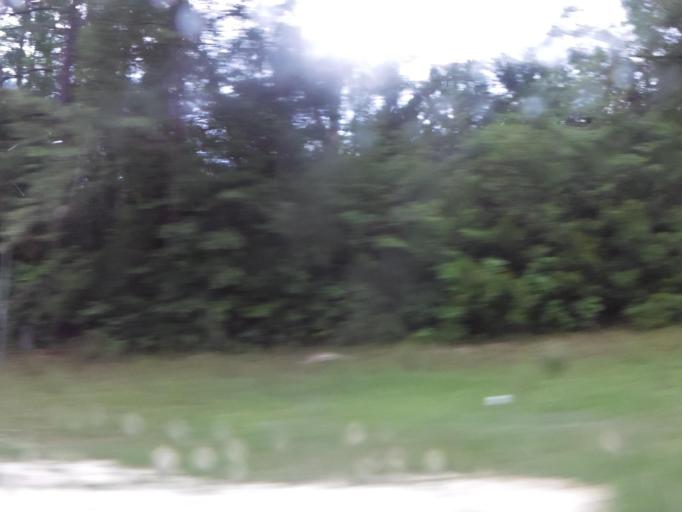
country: US
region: Florida
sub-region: Baker County
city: Macclenny
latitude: 30.2686
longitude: -82.1610
